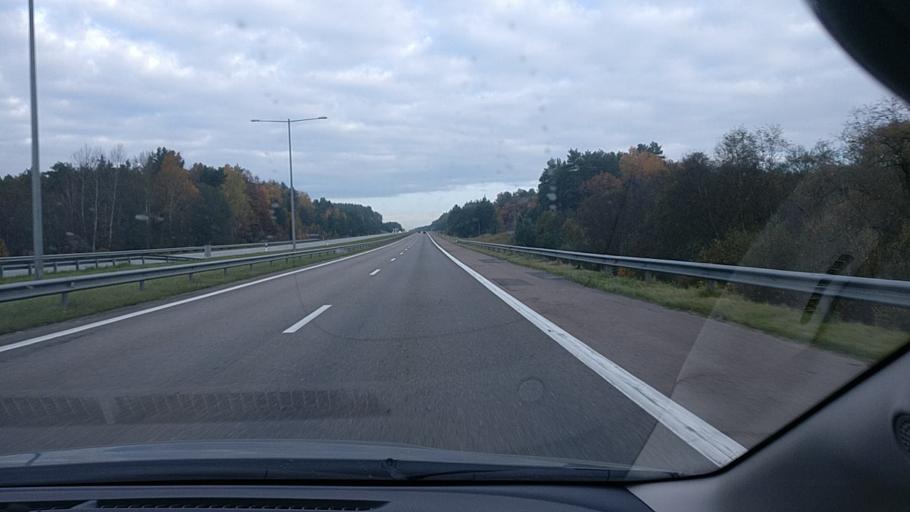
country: LT
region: Vilnius County
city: Ukmerge
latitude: 55.2556
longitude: 24.8164
